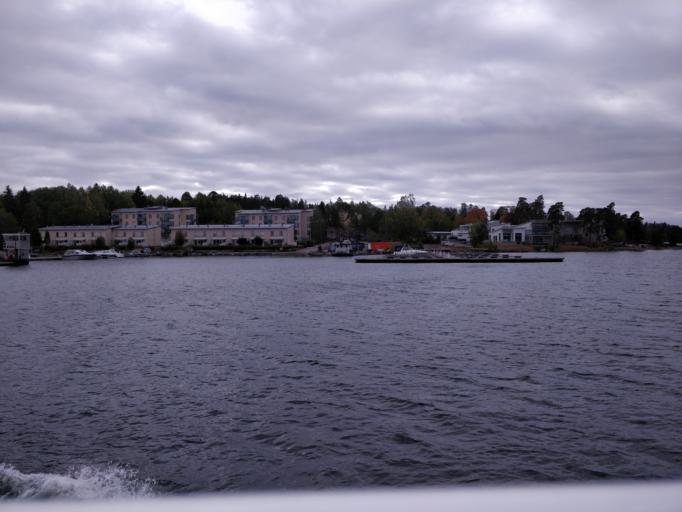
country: FI
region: Uusimaa
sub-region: Helsinki
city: Vantaa
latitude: 60.1740
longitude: 25.0839
